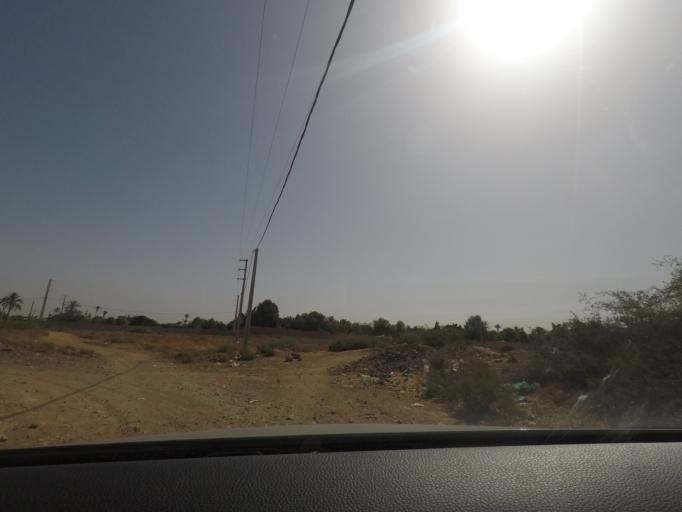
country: MA
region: Marrakech-Tensift-Al Haouz
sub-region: Marrakech
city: Marrakesh
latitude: 31.5794
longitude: -8.0242
